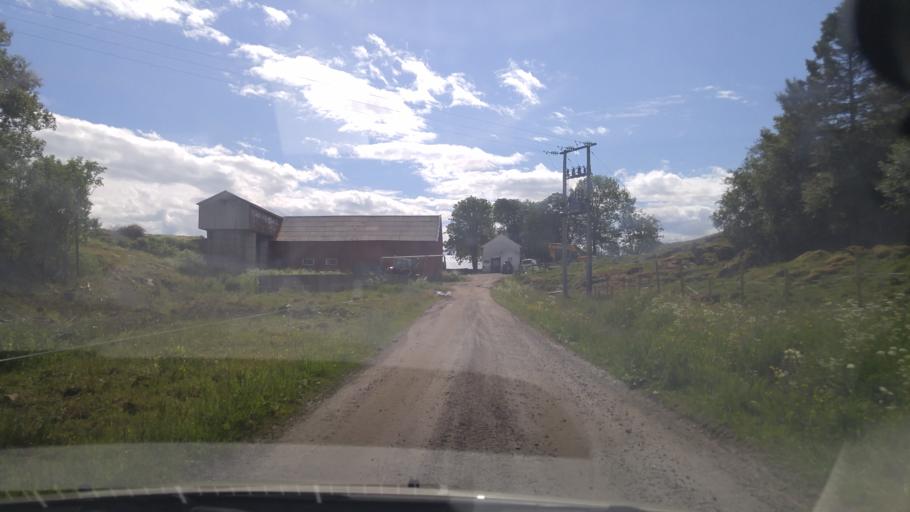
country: NO
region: Nord-Trondelag
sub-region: Vikna
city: Rorvik
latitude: 64.8943
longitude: 11.1082
